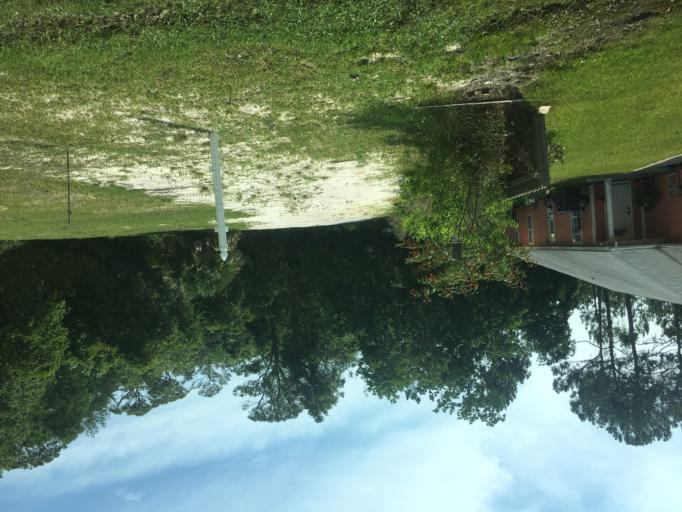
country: US
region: Florida
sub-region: Bay County
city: Laguna Beach
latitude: 30.2472
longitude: -85.9179
